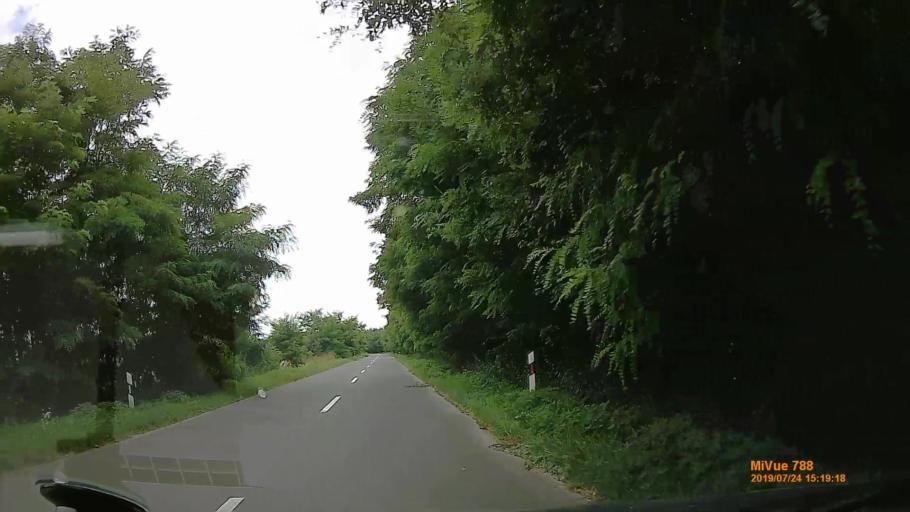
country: HU
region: Szabolcs-Szatmar-Bereg
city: Tarpa
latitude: 48.1714
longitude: 22.5439
